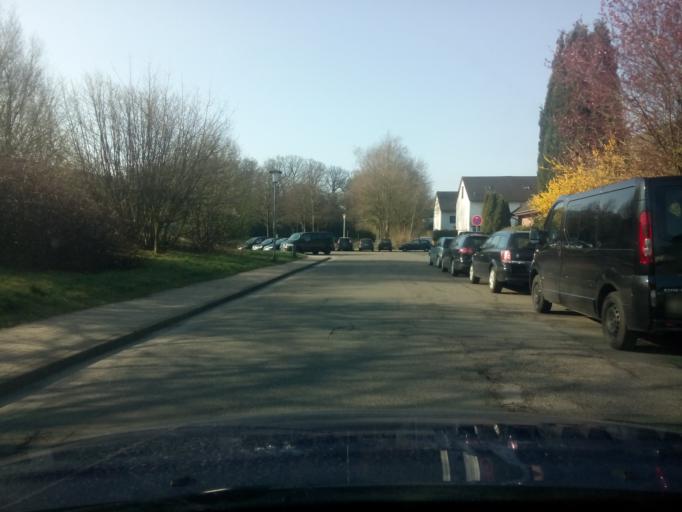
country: DE
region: Lower Saxony
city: Osterholz-Scharmbeck
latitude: 53.2303
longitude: 8.7688
